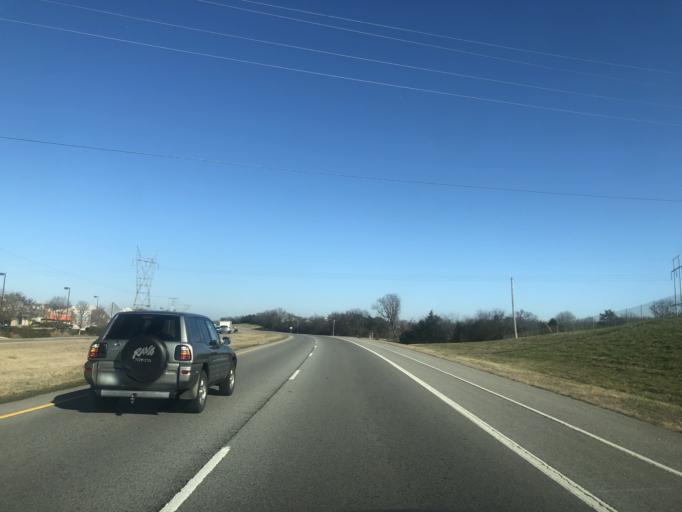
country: US
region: Tennessee
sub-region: Rutherford County
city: Smyrna
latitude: 35.9395
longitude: -86.5272
